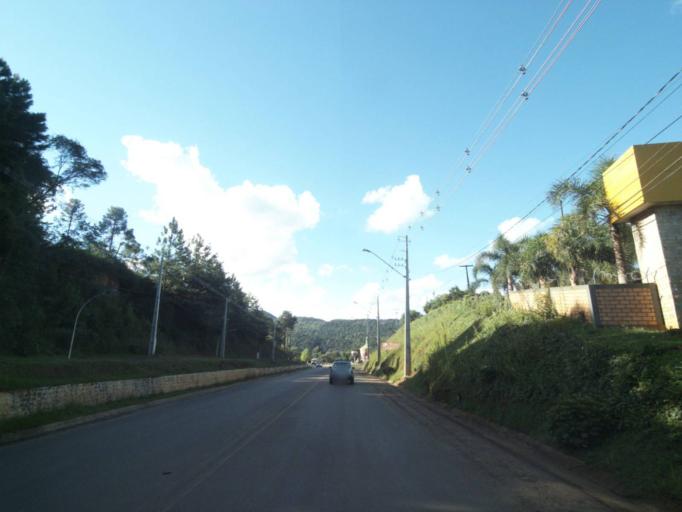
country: BR
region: Parana
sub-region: Uniao Da Vitoria
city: Uniao da Vitoria
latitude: -26.1549
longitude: -51.5425
